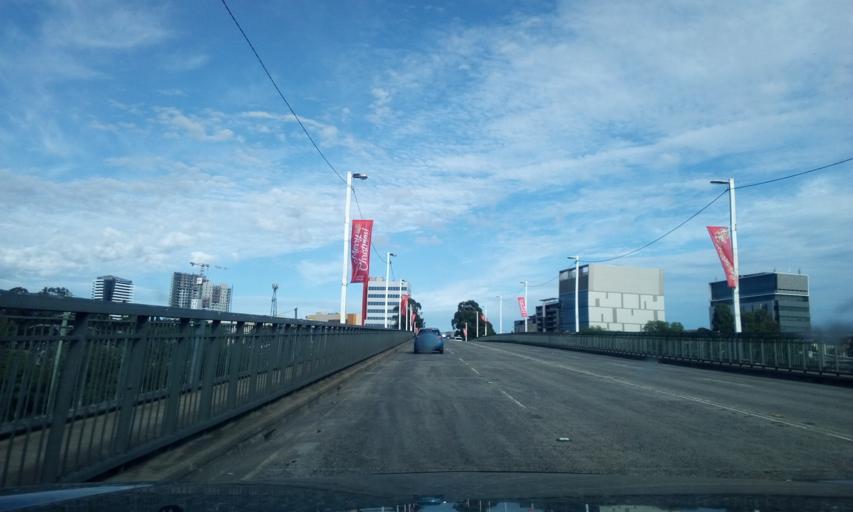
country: AU
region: New South Wales
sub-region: Fairfield
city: Liverpool
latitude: -33.9271
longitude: 150.9284
